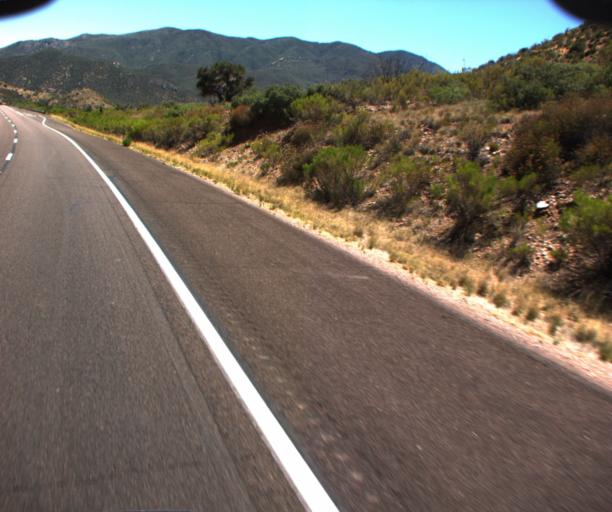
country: US
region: Arizona
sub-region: Gila County
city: Tonto Basin
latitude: 33.9789
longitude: -111.3861
